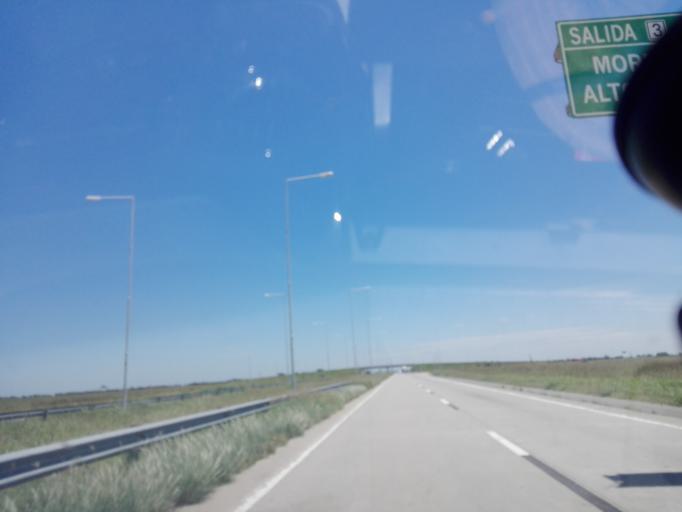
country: AR
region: Cordoba
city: Morrison
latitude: -32.5626
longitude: -62.8154
